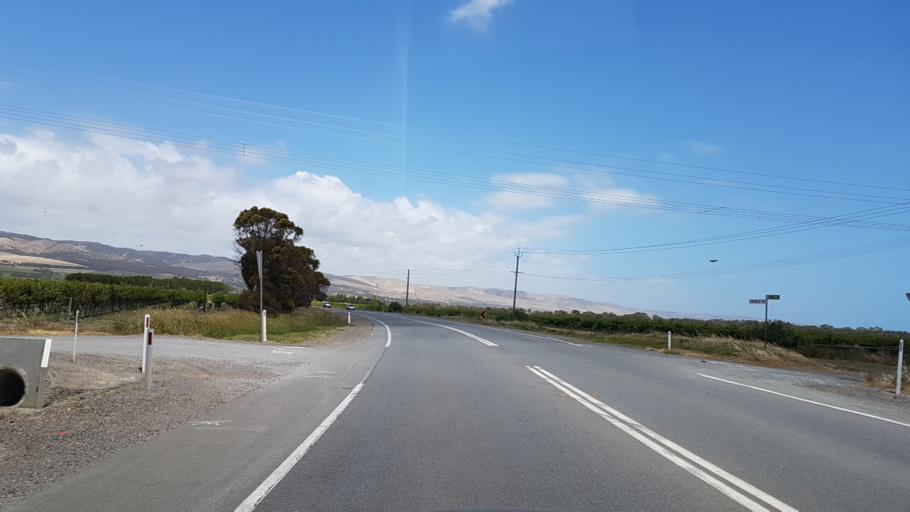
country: AU
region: South Australia
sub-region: Onkaparinga
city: Aldinga
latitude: -35.2862
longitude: 138.4720
